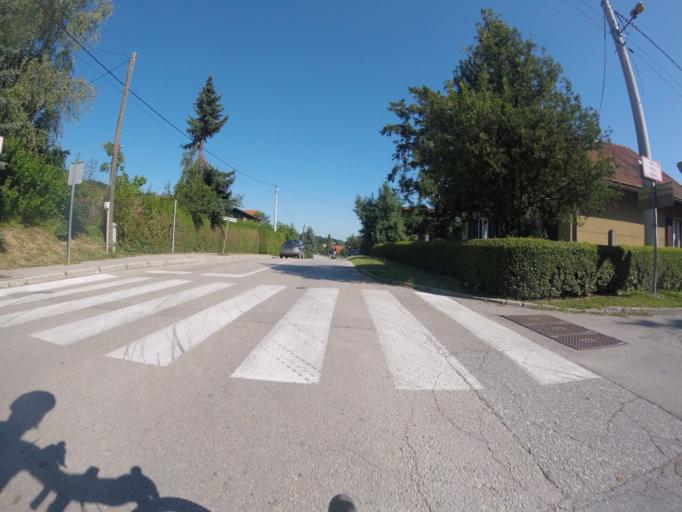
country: HR
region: Zagrebacka
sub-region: Grad Samobor
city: Samobor
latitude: 45.8181
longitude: 15.7024
